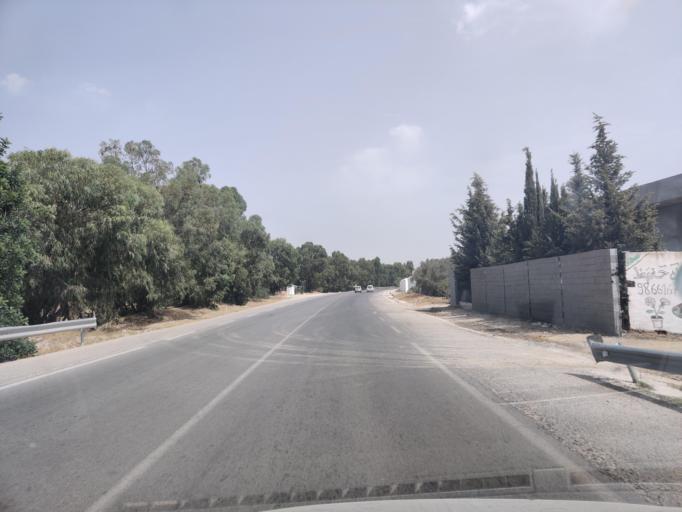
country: TN
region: Nabul
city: Al Hammamat
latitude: 36.4568
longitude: 10.5709
